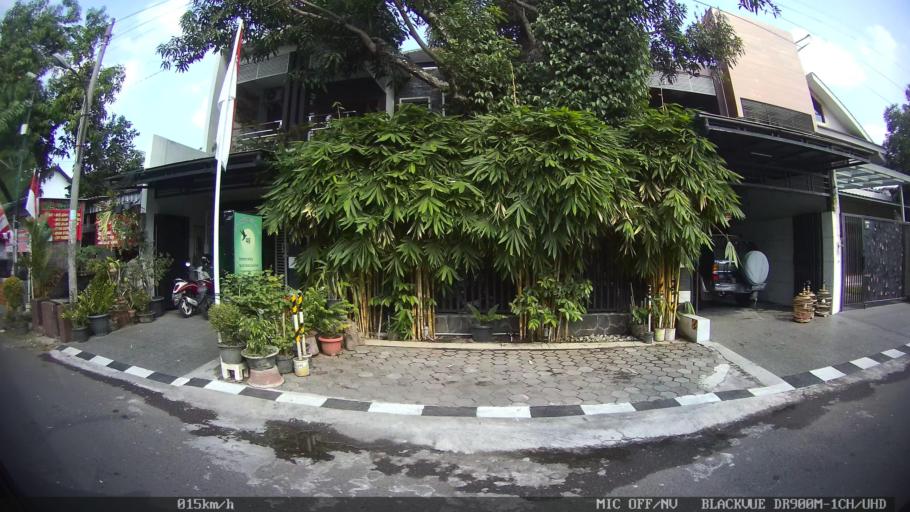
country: ID
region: Daerah Istimewa Yogyakarta
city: Yogyakarta
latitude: -7.7778
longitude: 110.3907
